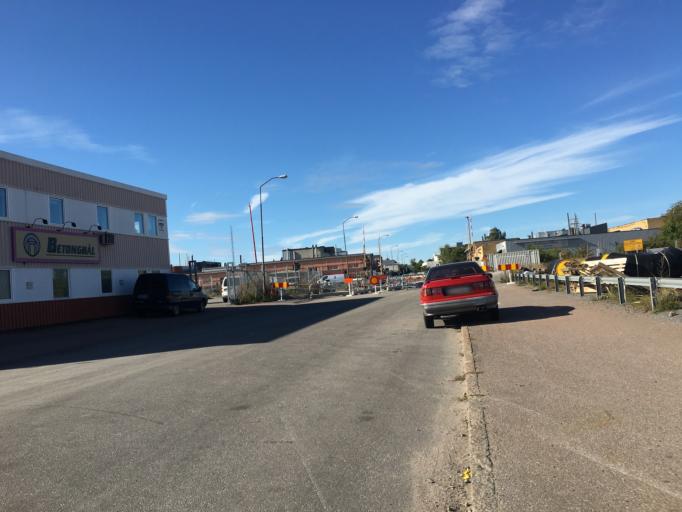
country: SE
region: Uppsala
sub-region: Uppsala Kommun
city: Uppsala
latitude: 59.8511
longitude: 17.6719
